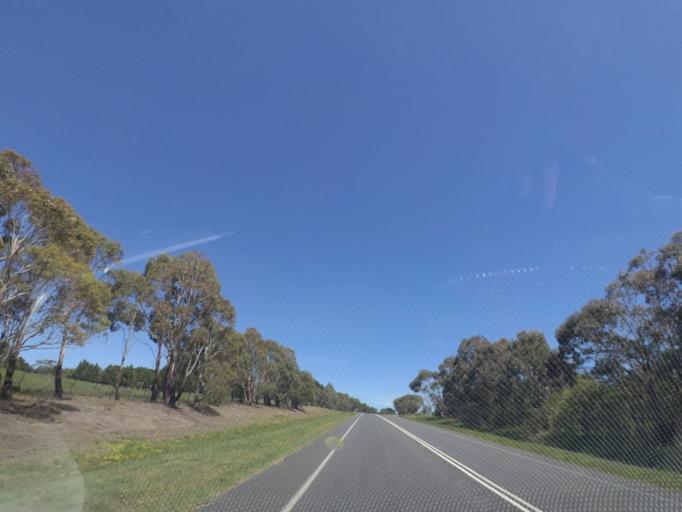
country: AU
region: Victoria
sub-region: Hume
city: Sunbury
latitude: -37.5420
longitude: 144.6360
